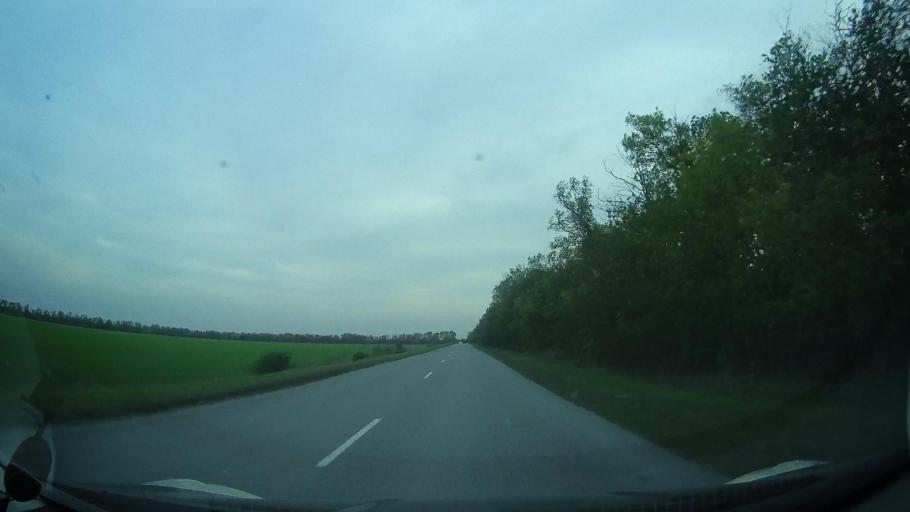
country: RU
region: Rostov
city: Kirovskaya
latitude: 47.0071
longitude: 39.9789
